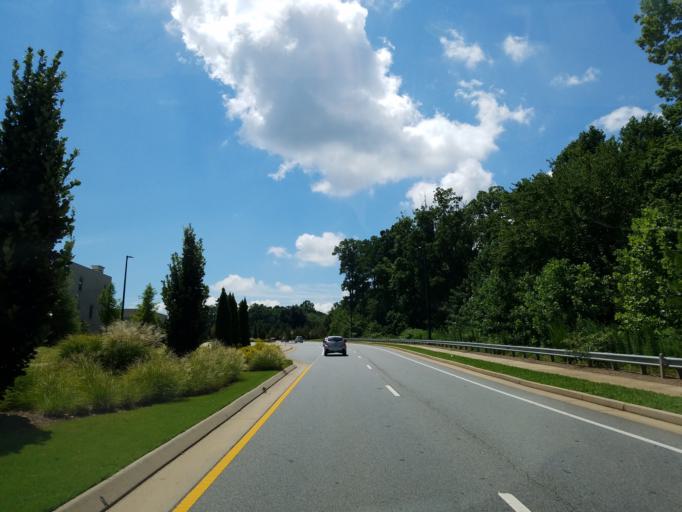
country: US
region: Georgia
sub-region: Fulton County
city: Alpharetta
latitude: 34.0725
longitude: -84.2779
